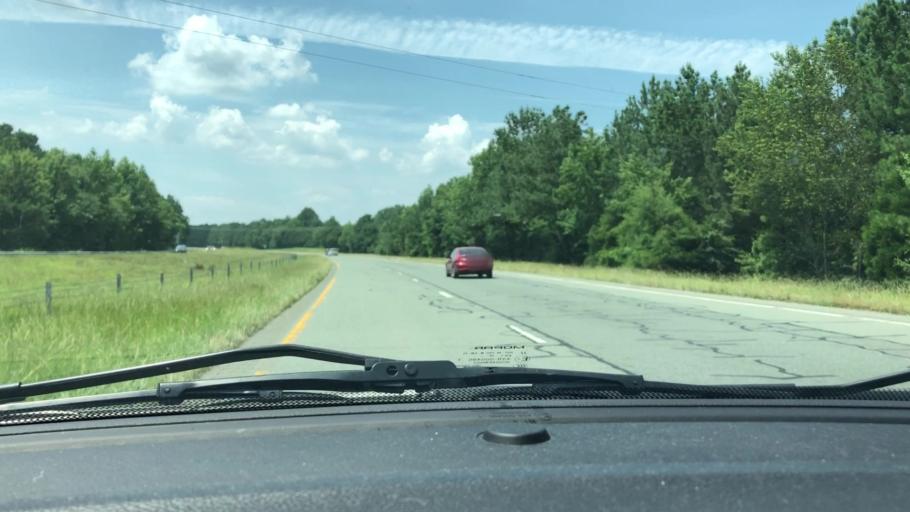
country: US
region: North Carolina
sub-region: Chatham County
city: Siler City
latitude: 35.7401
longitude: -79.4345
